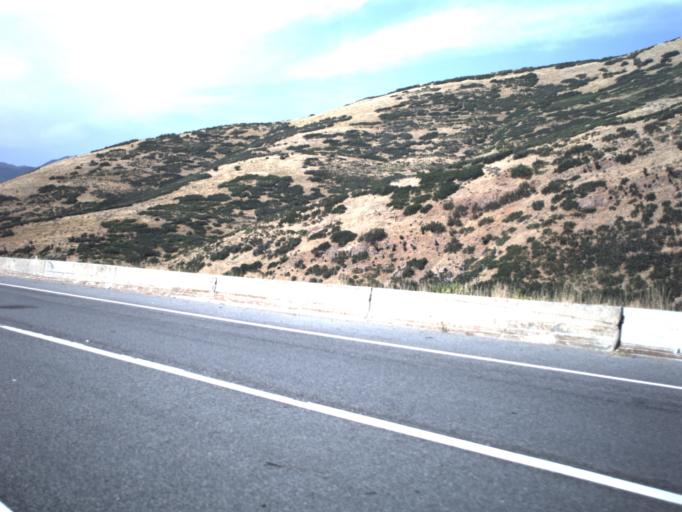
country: US
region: Utah
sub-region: Summit County
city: Summit Park
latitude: 40.7412
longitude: -111.6757
